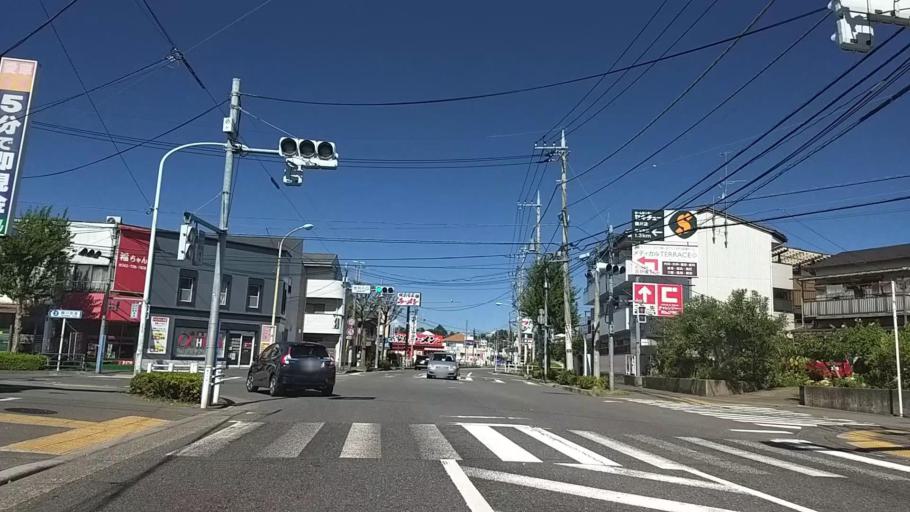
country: JP
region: Tokyo
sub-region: Machida-shi
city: Machida
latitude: 35.5844
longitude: 139.4729
